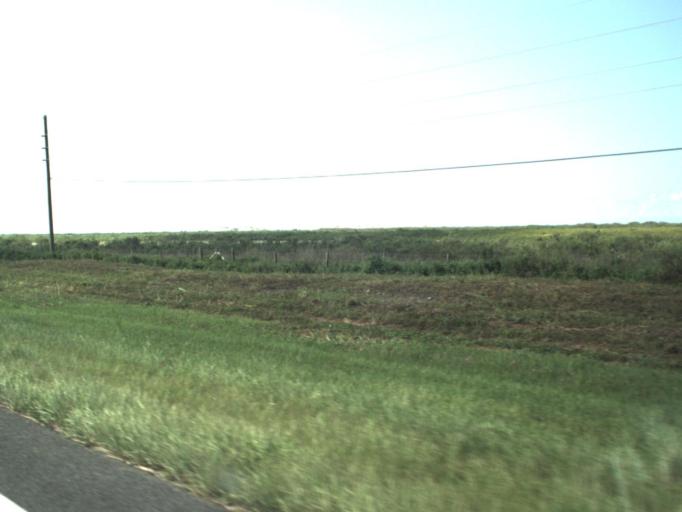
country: US
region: Florida
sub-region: Palm Beach County
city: Belle Glade Camp
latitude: 26.4780
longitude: -80.6488
